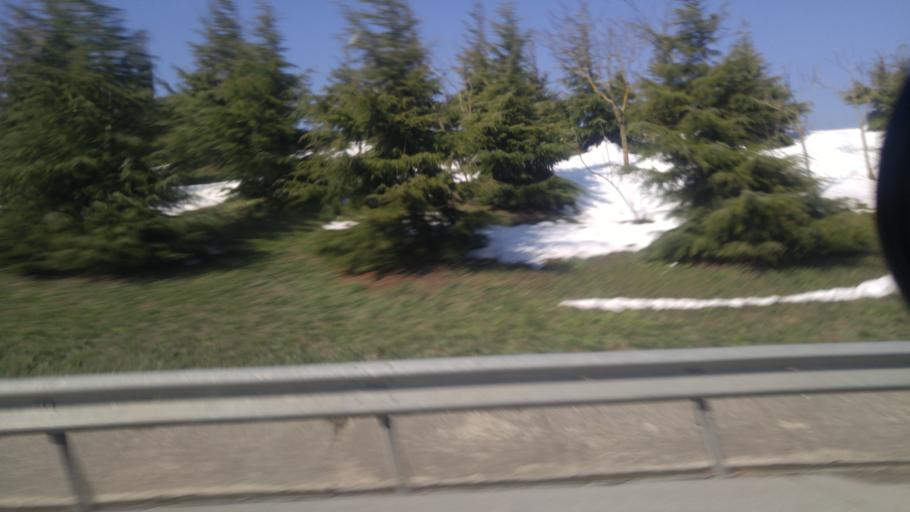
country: TR
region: Istanbul
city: Celaliye
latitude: 41.0544
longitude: 28.4553
